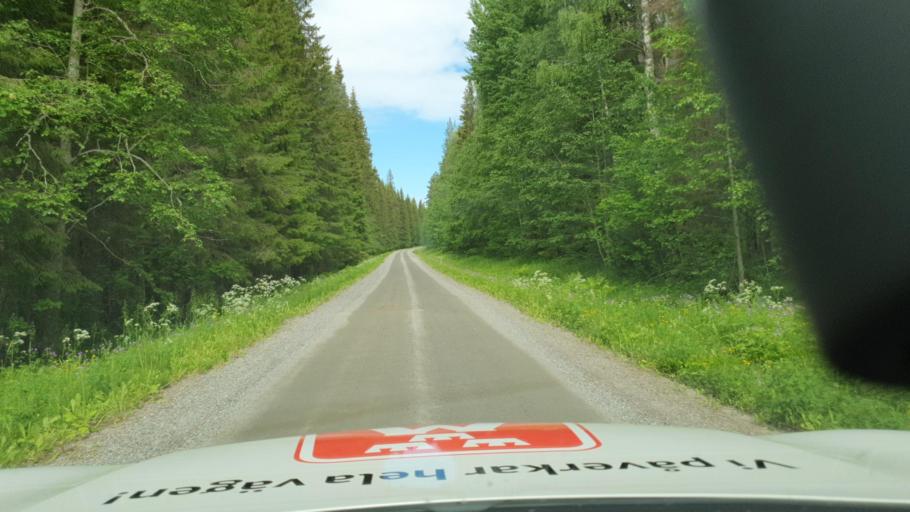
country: SE
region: Vaesterbotten
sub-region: Skelleftea Kommun
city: Forsbacka
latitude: 64.6400
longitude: 20.5443
